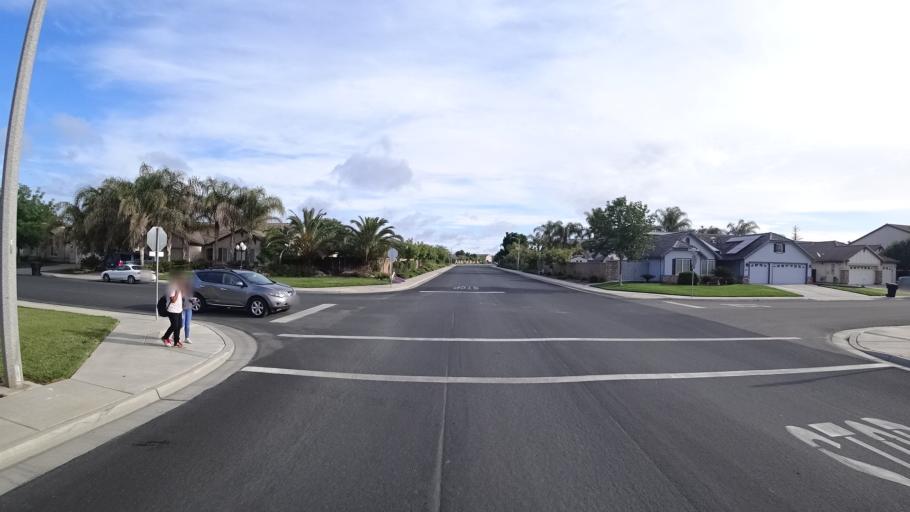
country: US
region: California
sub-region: Kings County
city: Hanford
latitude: 36.3454
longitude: -119.6784
